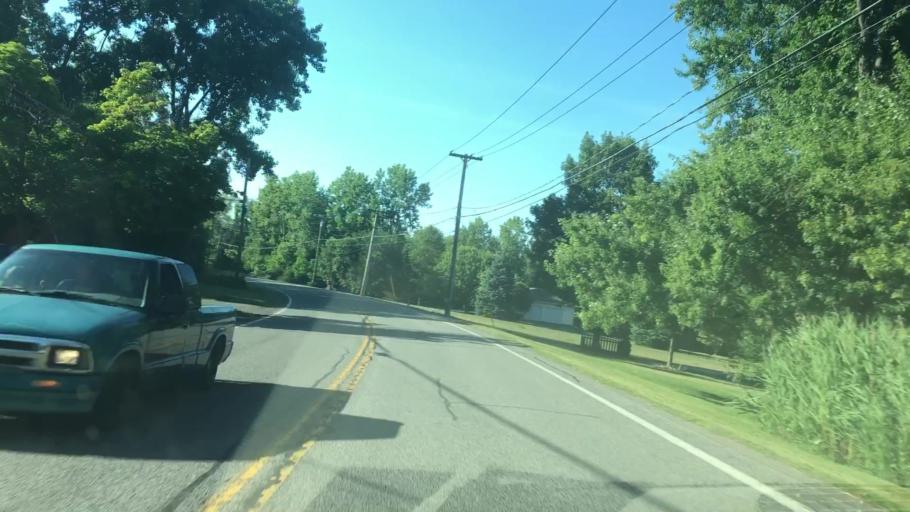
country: US
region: New York
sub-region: Wayne County
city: Ontario
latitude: 43.1795
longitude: -77.2856
